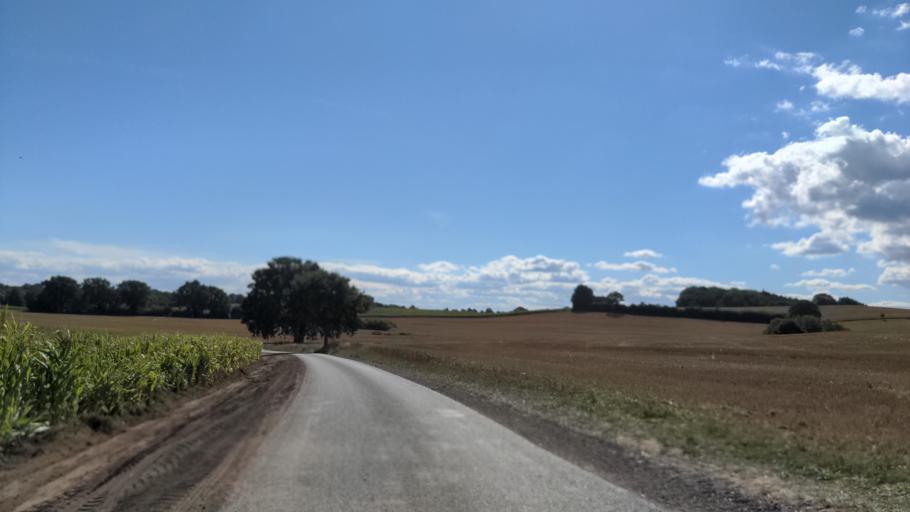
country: DE
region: Schleswig-Holstein
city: Kasseedorf
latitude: 54.1313
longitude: 10.7194
